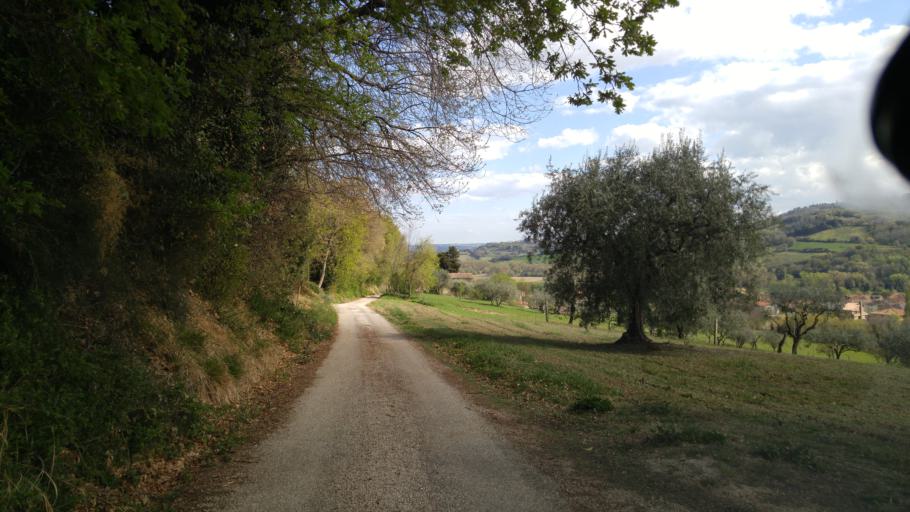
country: IT
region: The Marches
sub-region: Provincia di Pesaro e Urbino
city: Fenile
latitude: 43.8455
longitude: 12.9621
